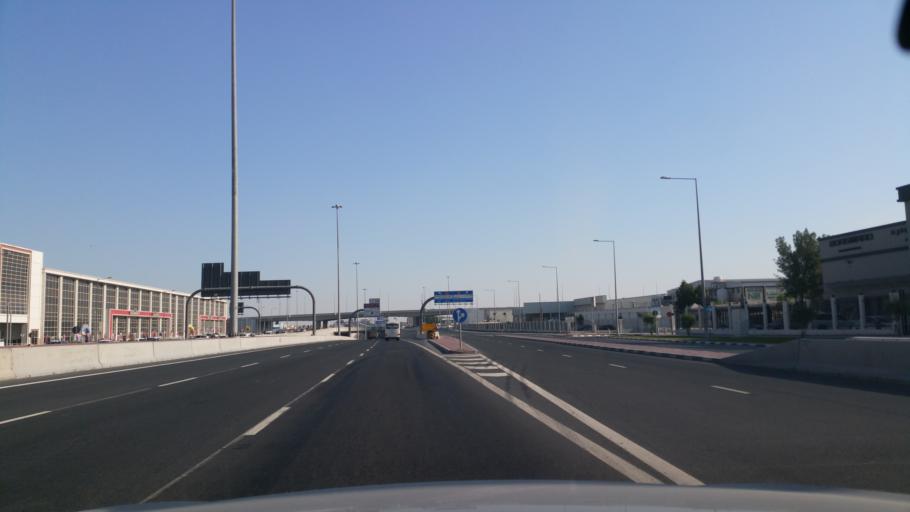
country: QA
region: Al Wakrah
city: Al Wukayr
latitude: 25.1964
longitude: 51.4525
